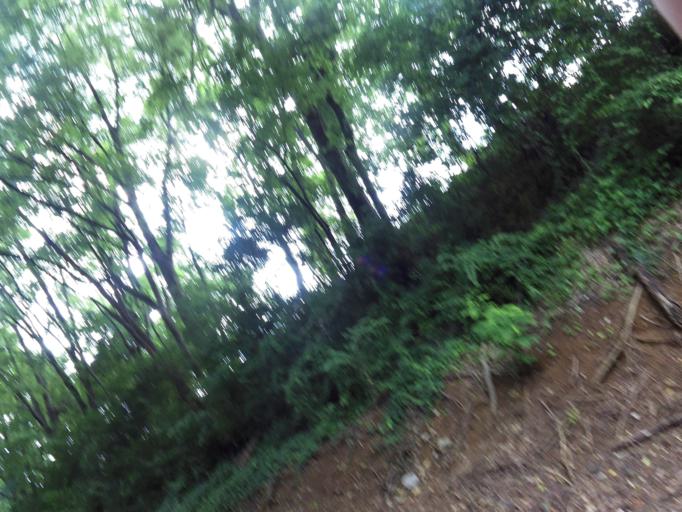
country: US
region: Tennessee
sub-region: Knox County
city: Knoxville
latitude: 35.9547
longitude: -83.9127
